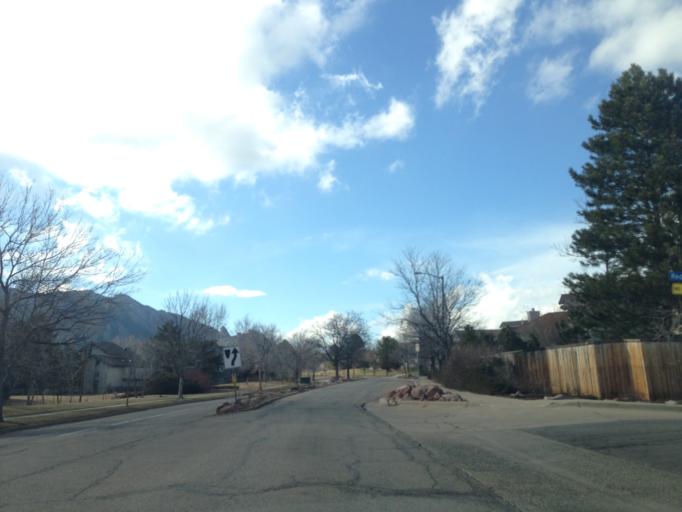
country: US
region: Colorado
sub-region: Boulder County
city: Boulder
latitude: 39.9649
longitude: -105.2539
